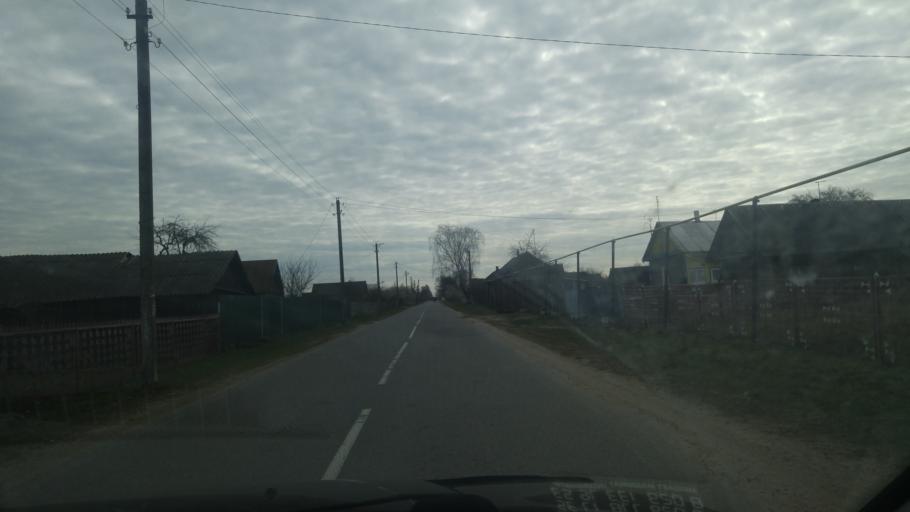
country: BY
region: Minsk
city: Pukhavichy
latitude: 53.5867
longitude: 28.2293
